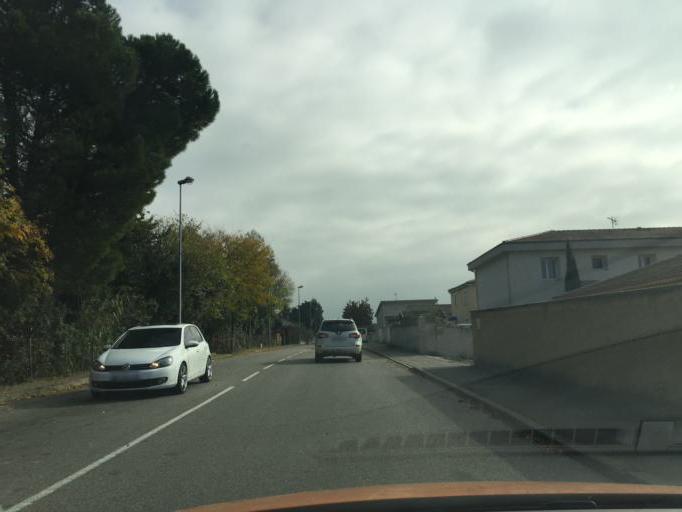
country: FR
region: Rhone-Alpes
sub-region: Departement de la Drome
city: Portes-les-Valence
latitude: 44.8814
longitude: 4.8786
